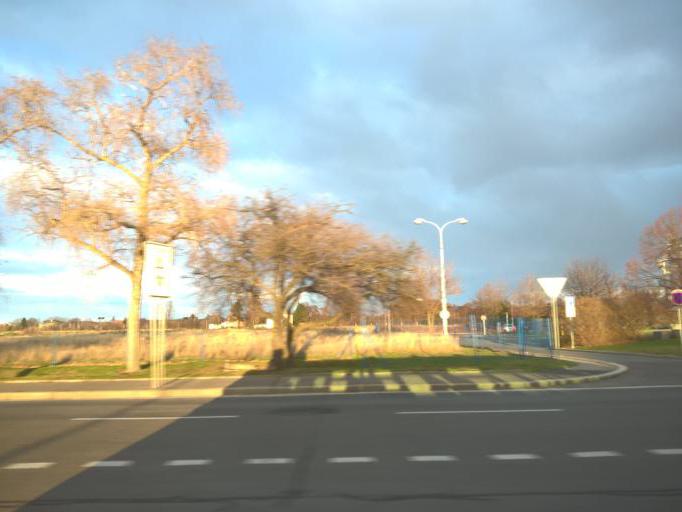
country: CZ
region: Central Bohemia
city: Hostivice
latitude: 50.0985
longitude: 14.2893
